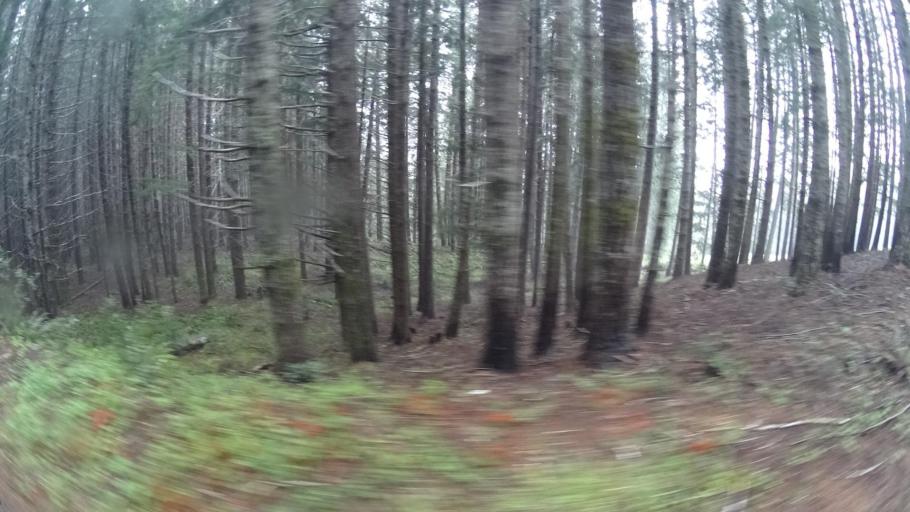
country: US
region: California
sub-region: Humboldt County
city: Westhaven-Moonstone
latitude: 41.2030
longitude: -123.9460
